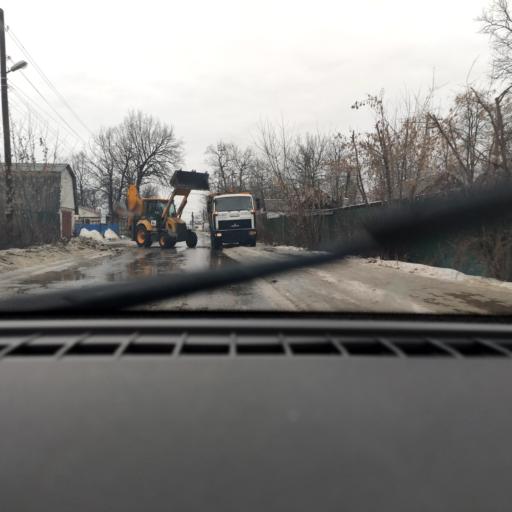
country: RU
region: Voronezj
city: Somovo
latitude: 51.7363
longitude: 39.3567
